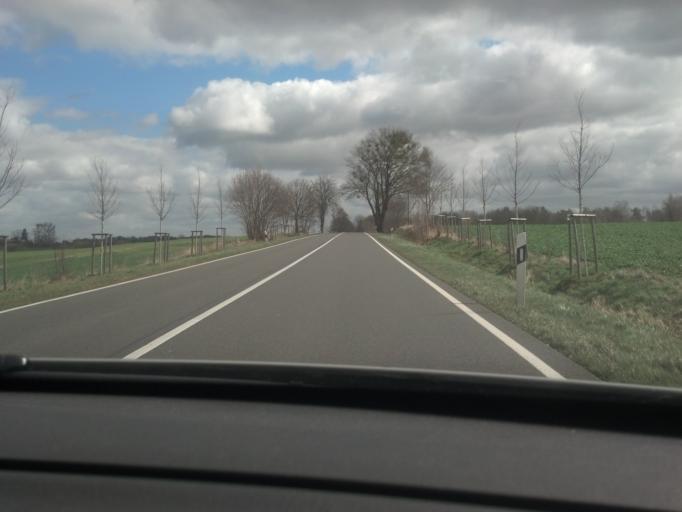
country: DE
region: Mecklenburg-Vorpommern
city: Rechlin
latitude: 53.3159
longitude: 12.7334
